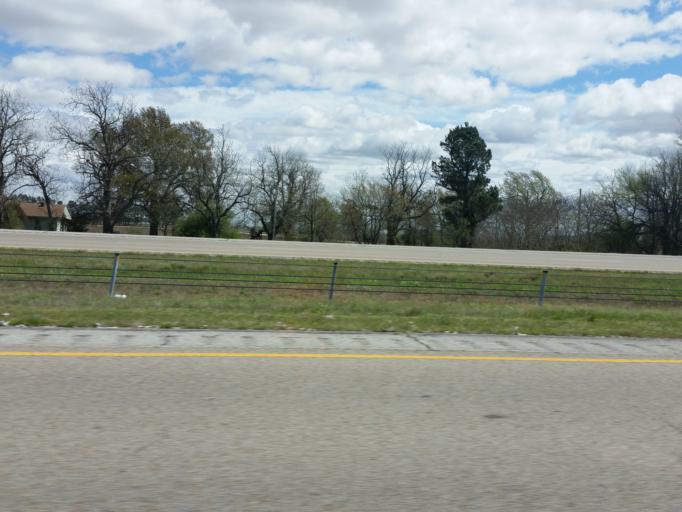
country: US
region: Arkansas
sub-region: Craighead County
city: Bay
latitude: 35.7636
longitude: -90.5768
